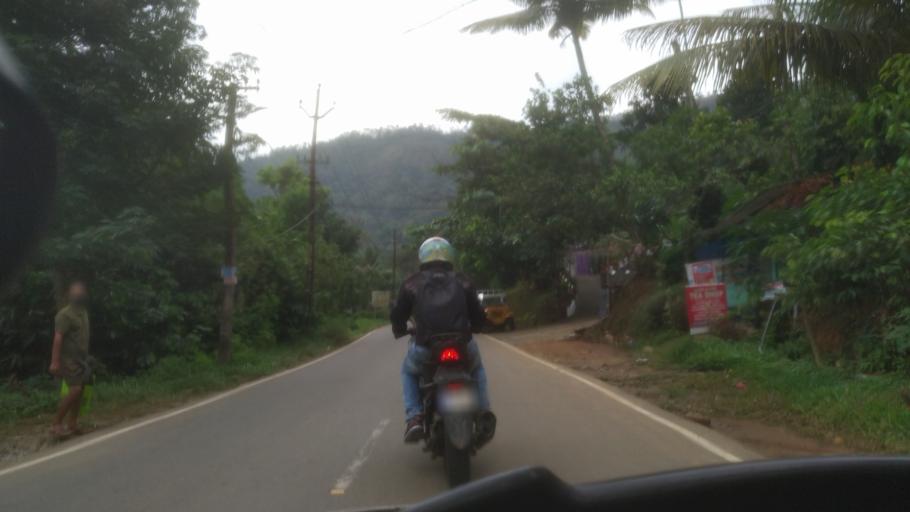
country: IN
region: Kerala
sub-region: Idukki
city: Munnar
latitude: 10.0006
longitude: 76.9688
